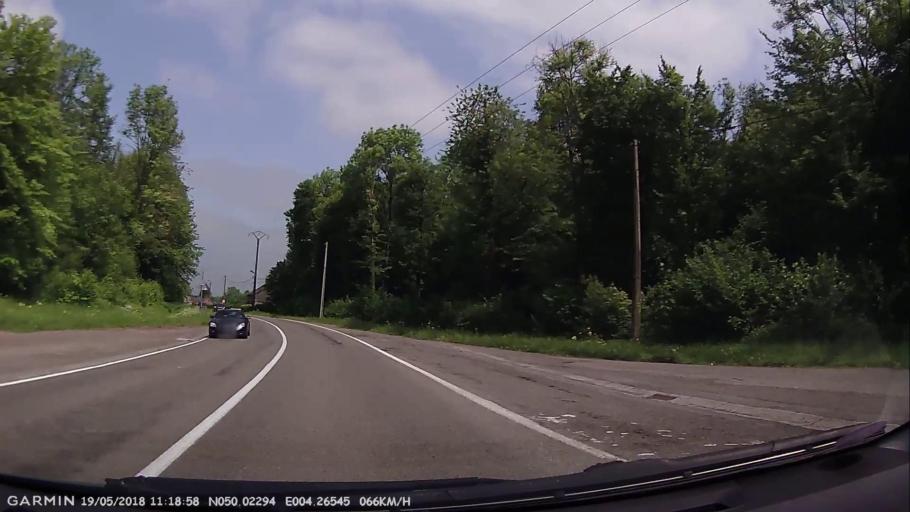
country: BE
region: Wallonia
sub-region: Province du Hainaut
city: Chimay
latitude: 50.0231
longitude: 4.2655
